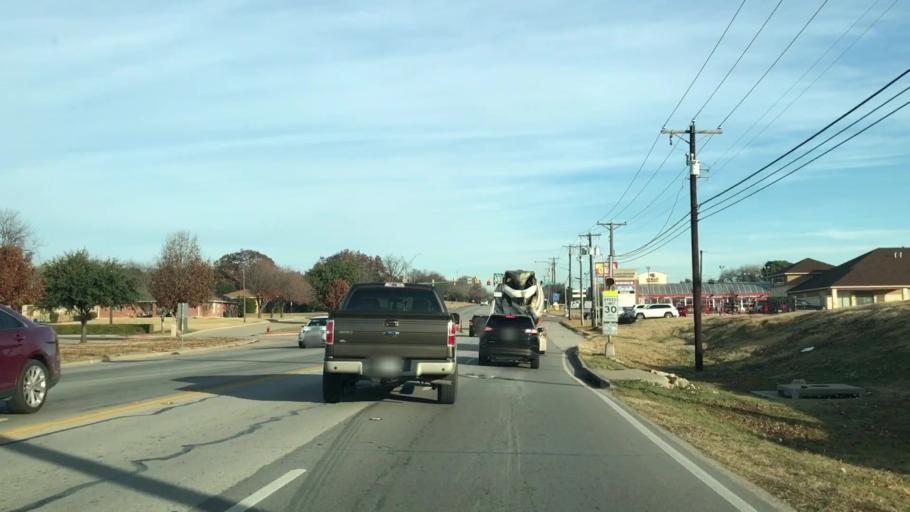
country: US
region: Texas
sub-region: Tarrant County
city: Sansom Park
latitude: 32.8163
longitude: -97.4199
